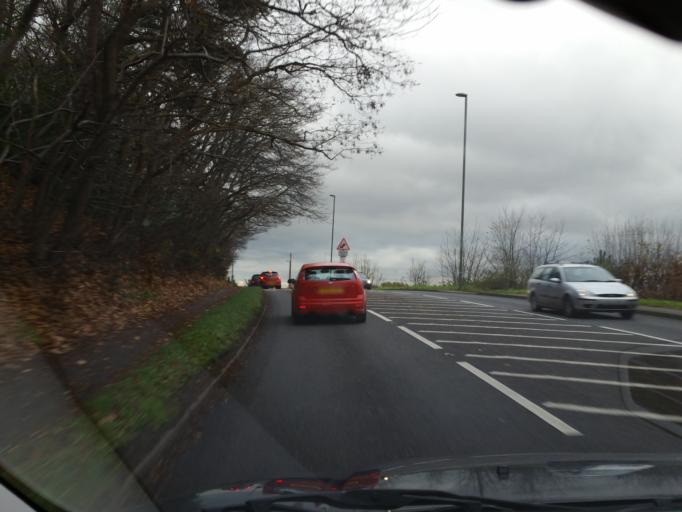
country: GB
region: England
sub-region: Surrey
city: Bagshot
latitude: 51.3542
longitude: -0.7021
